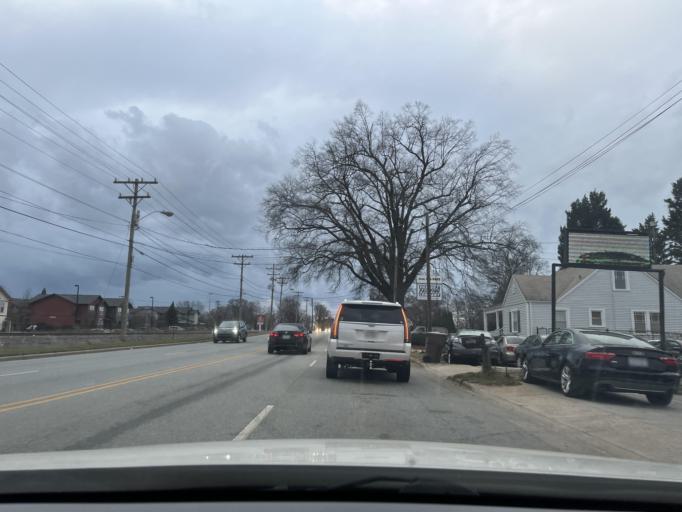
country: US
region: North Carolina
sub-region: Guilford County
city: Greensboro
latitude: 36.0607
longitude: -79.8528
